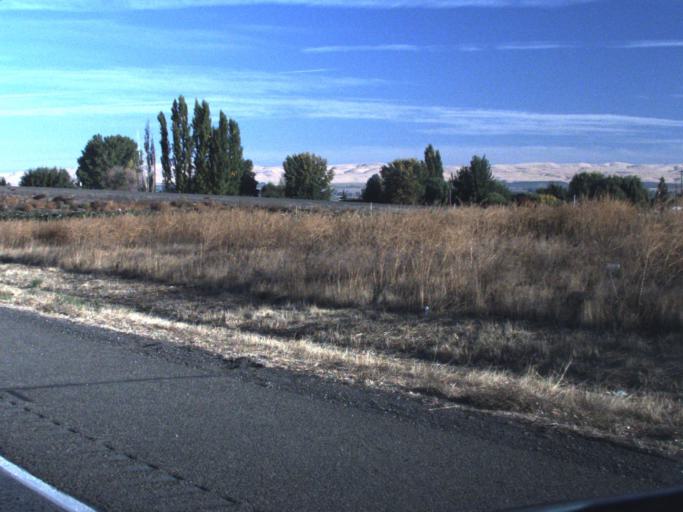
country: US
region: Washington
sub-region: Yakima County
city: Sunnyside
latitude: 46.3151
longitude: -120.0531
